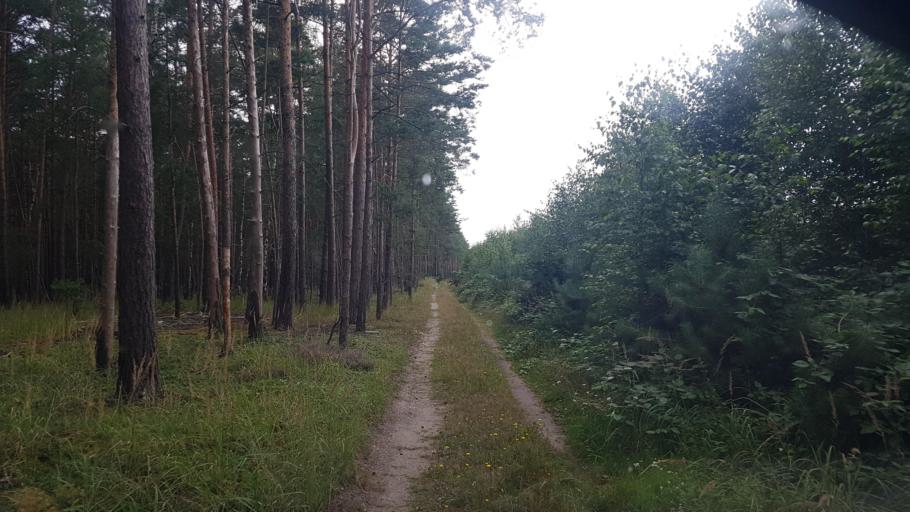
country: DE
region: Brandenburg
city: Sallgast
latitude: 51.5823
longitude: 13.9102
